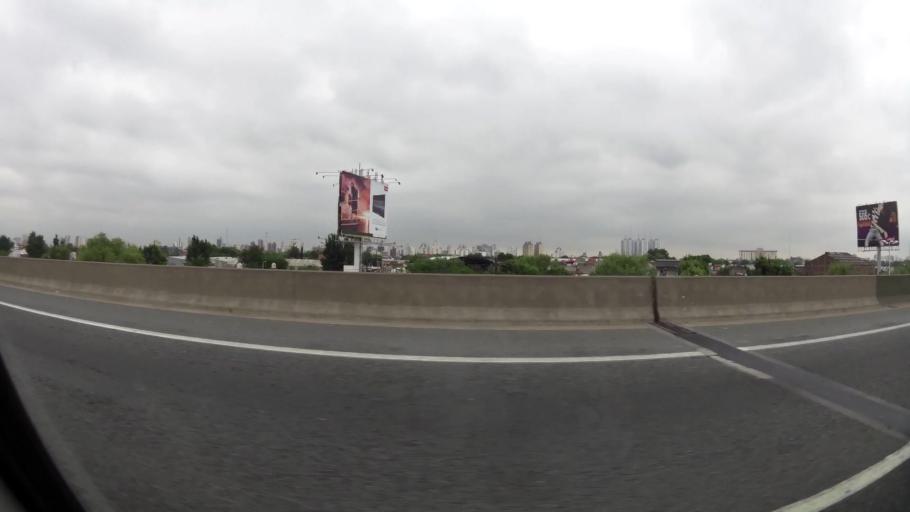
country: AR
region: Buenos Aires
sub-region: Partido de Avellaneda
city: Avellaneda
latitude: -34.6553
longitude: -58.3519
